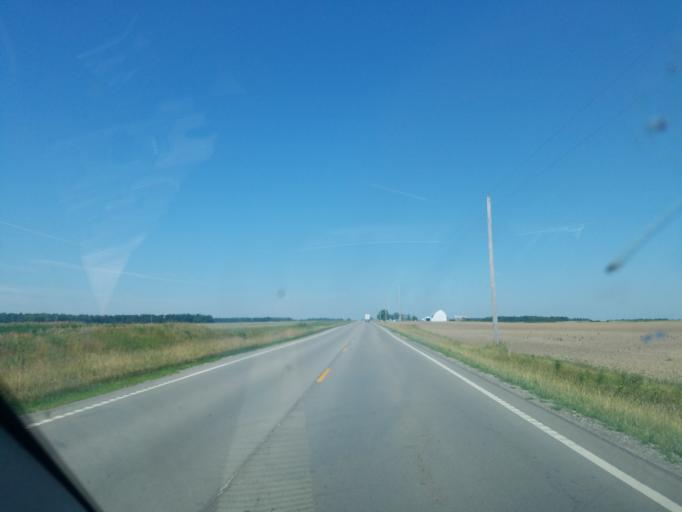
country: US
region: Ohio
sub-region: Logan County
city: Lakeview
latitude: 40.4393
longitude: -83.9690
